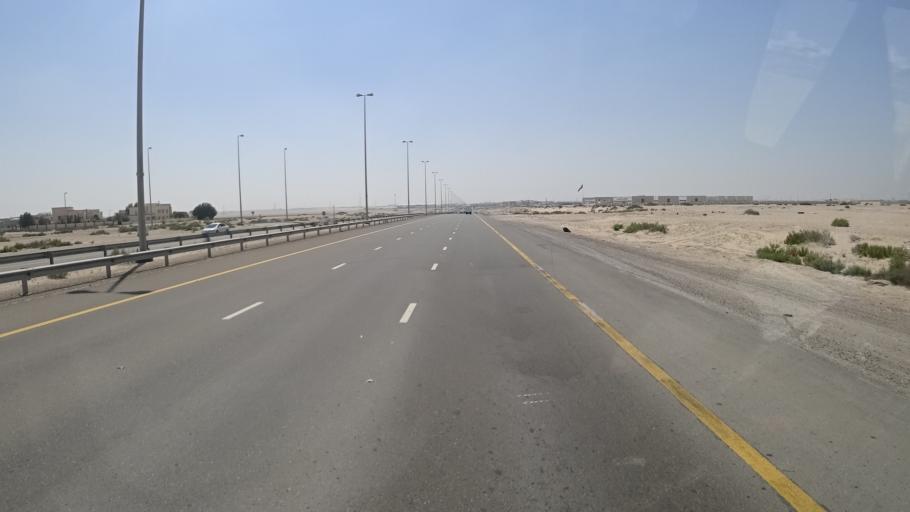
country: AE
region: Abu Dhabi
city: Abu Dhabi
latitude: 24.3263
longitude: 54.6891
